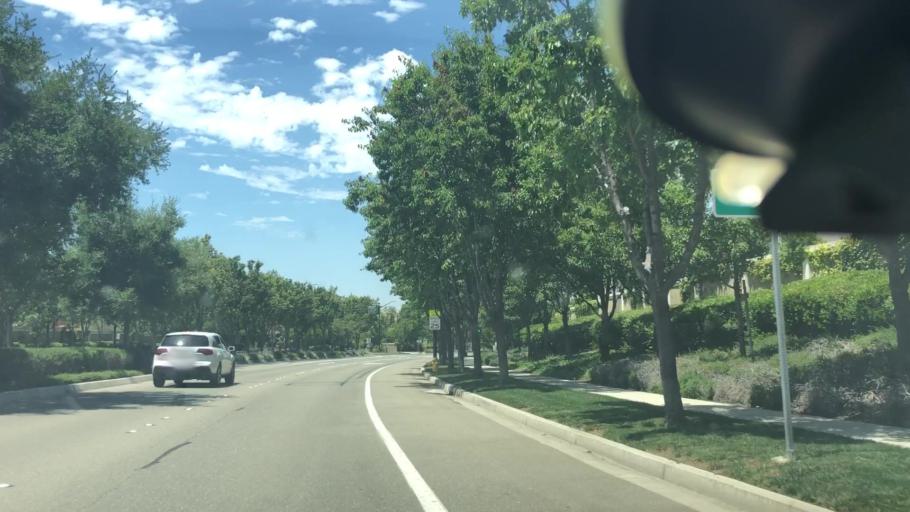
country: US
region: California
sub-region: Alameda County
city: Dublin
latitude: 37.7495
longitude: -121.8949
